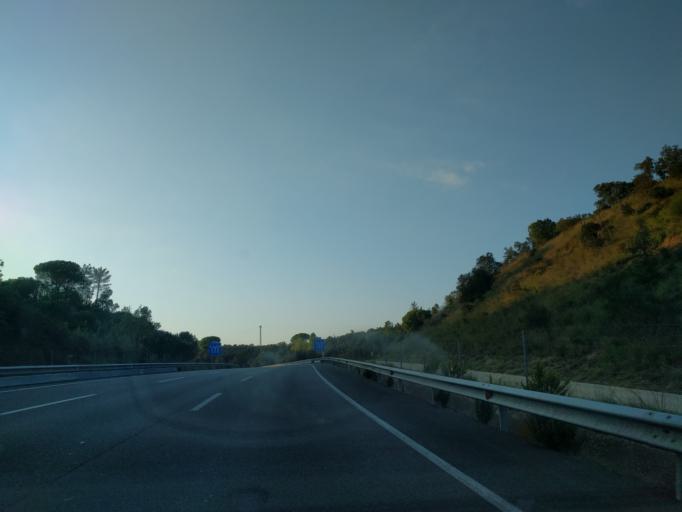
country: ES
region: Catalonia
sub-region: Provincia de Girona
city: Llagostera
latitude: 41.8296
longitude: 2.9379
